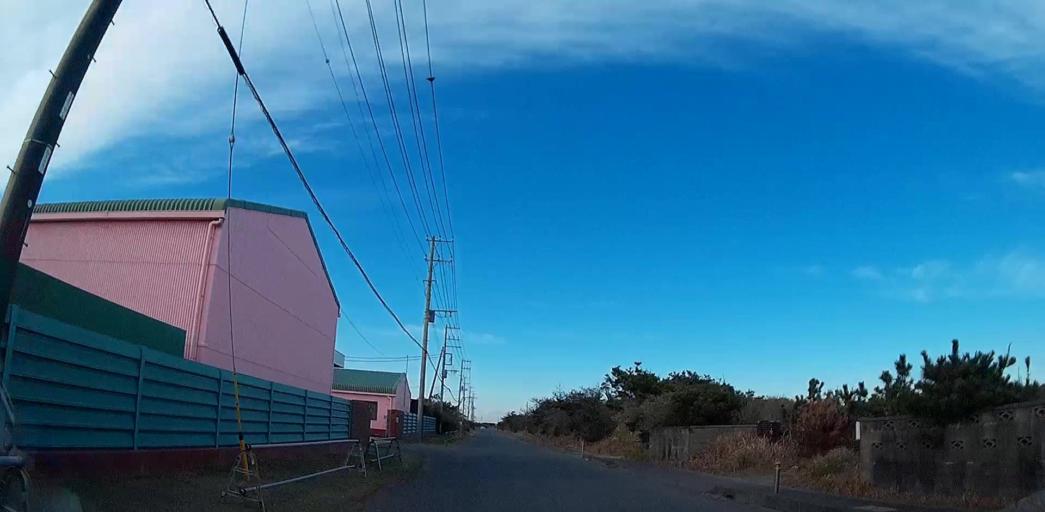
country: JP
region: Chiba
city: Hasaki
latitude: 35.7703
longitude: 140.8147
